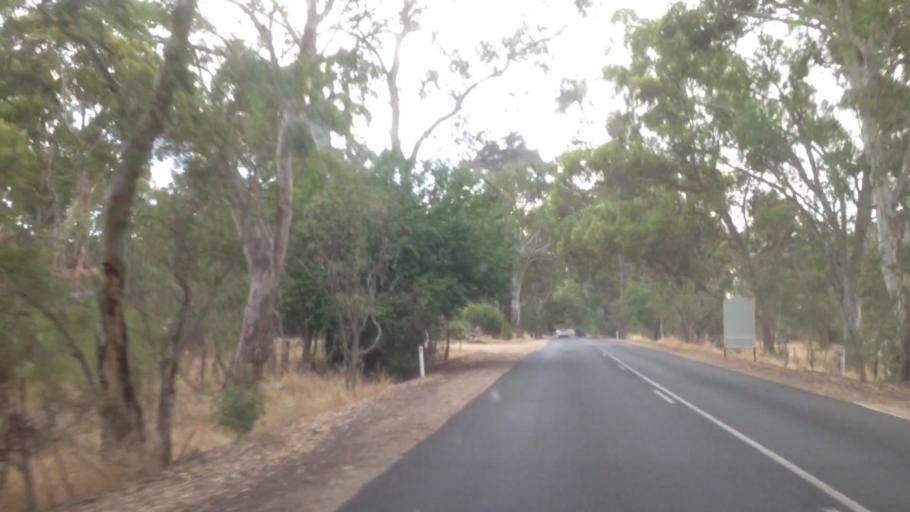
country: AU
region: South Australia
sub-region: Barossa
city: Williamstown
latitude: -34.6664
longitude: 138.8738
